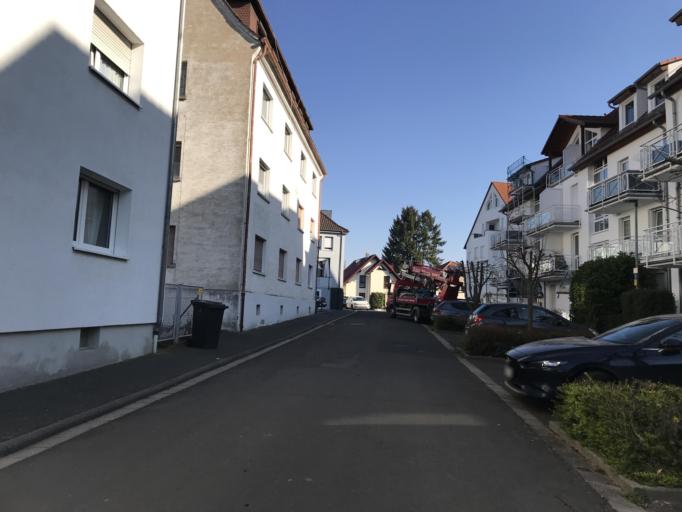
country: DE
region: Hesse
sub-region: Regierungsbezirk Darmstadt
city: Butzbach
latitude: 50.4301
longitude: 8.6583
